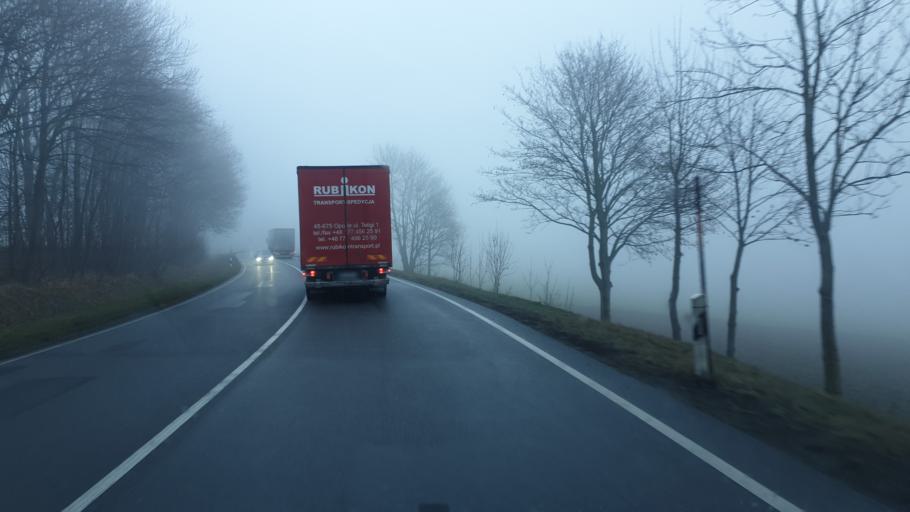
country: DE
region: Saxony
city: Grossolbersdorf
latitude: 50.6843
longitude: 13.1166
